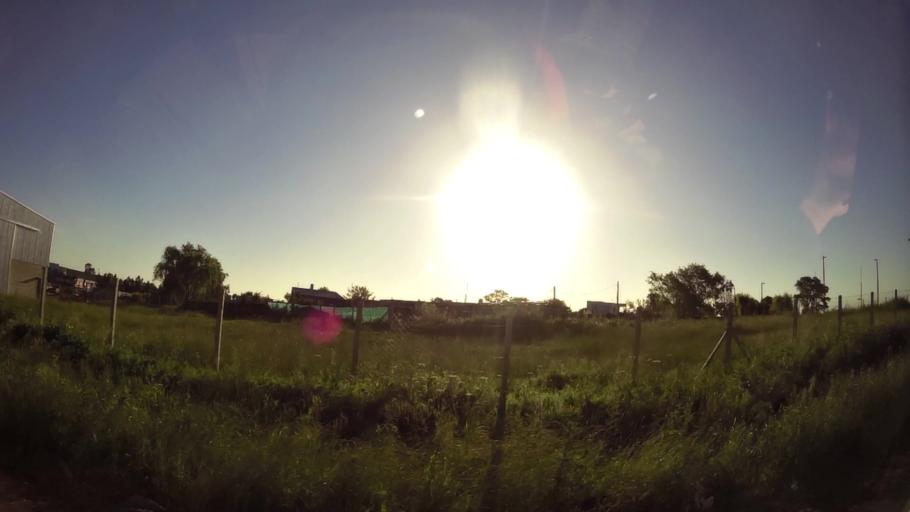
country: UY
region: Canelones
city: La Paz
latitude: -34.8266
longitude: -56.2456
